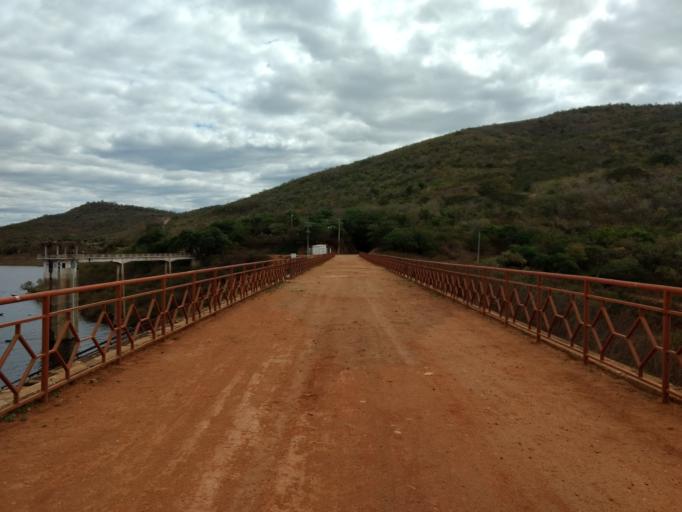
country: BR
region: Ceara
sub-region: Pentecoste
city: Pentecoste
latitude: -4.0623
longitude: -39.4542
